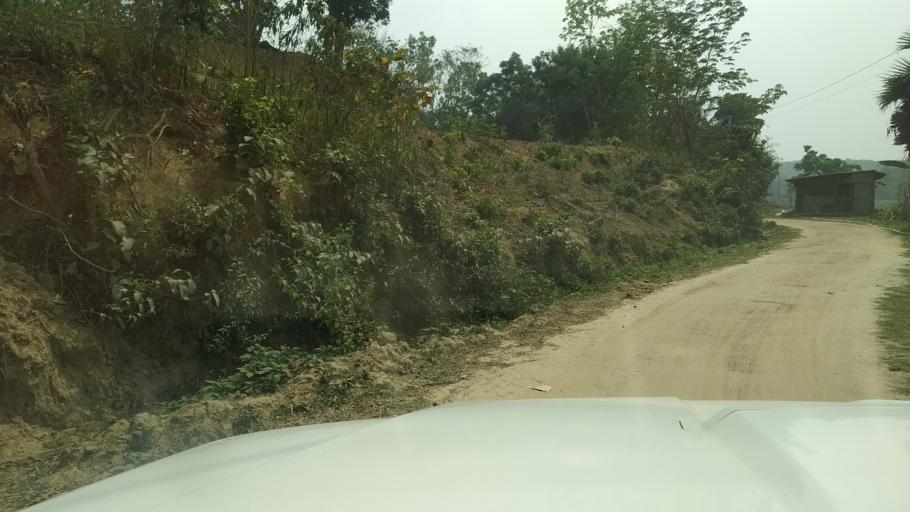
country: IN
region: Tripura
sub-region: West Tripura
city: Sonamura
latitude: 23.4307
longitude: 91.3128
